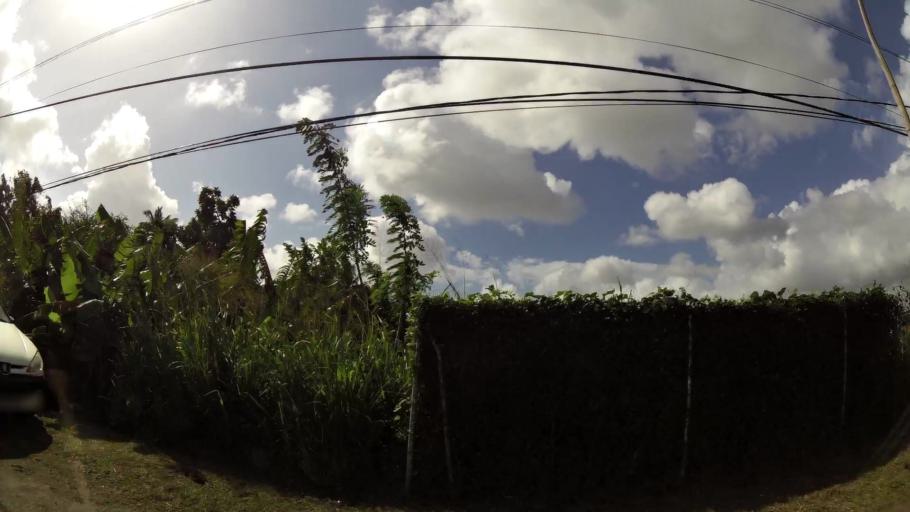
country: MQ
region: Martinique
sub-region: Martinique
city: Le Lamentin
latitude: 14.6139
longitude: -61.0049
